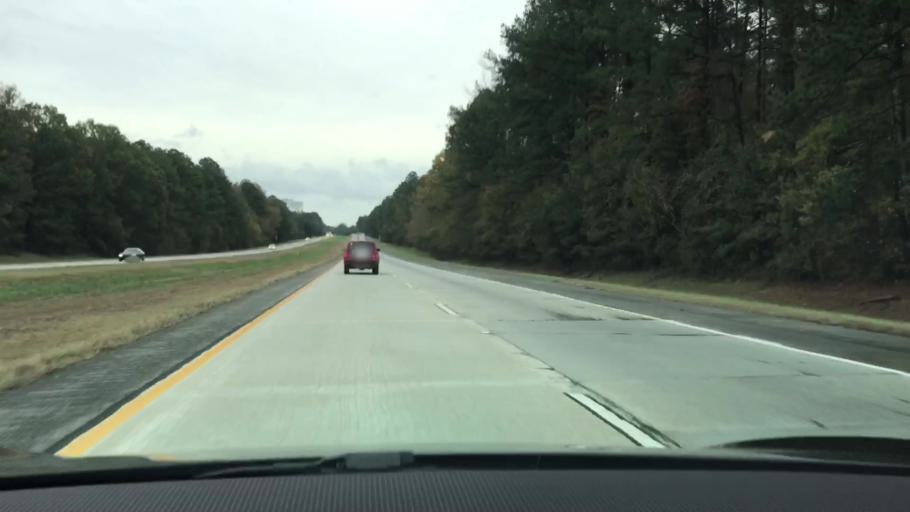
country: US
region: Georgia
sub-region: Taliaferro County
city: Crawfordville
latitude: 33.5293
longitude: -82.9696
